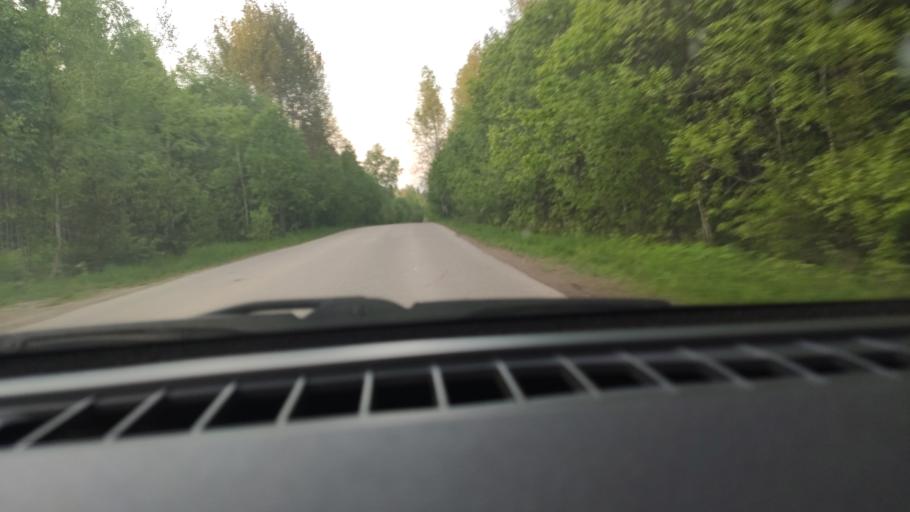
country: RU
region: Perm
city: Overyata
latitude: 58.0732
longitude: 56.0014
